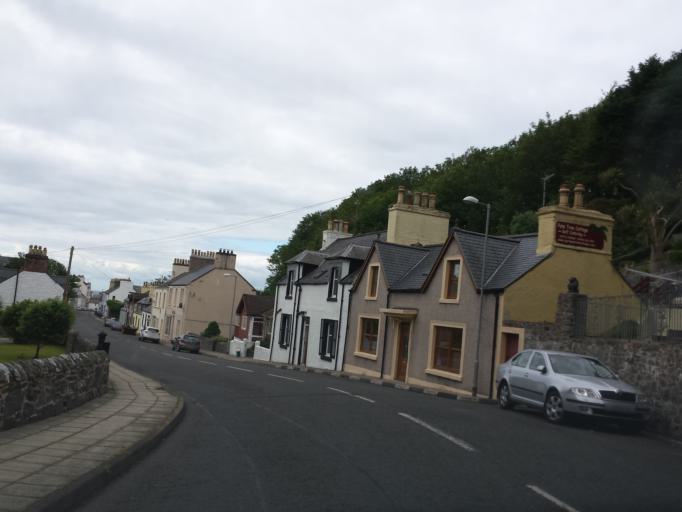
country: GB
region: Scotland
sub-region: Dumfries and Galloway
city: Stranraer
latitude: 54.8448
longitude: -5.1142
